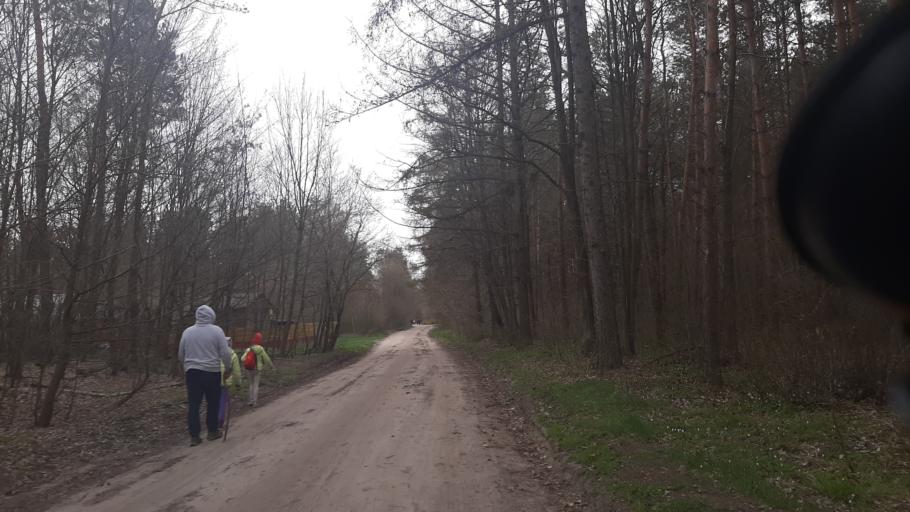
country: PL
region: Lublin Voivodeship
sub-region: Powiat lubelski
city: Niemce
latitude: 51.3915
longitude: 22.5659
